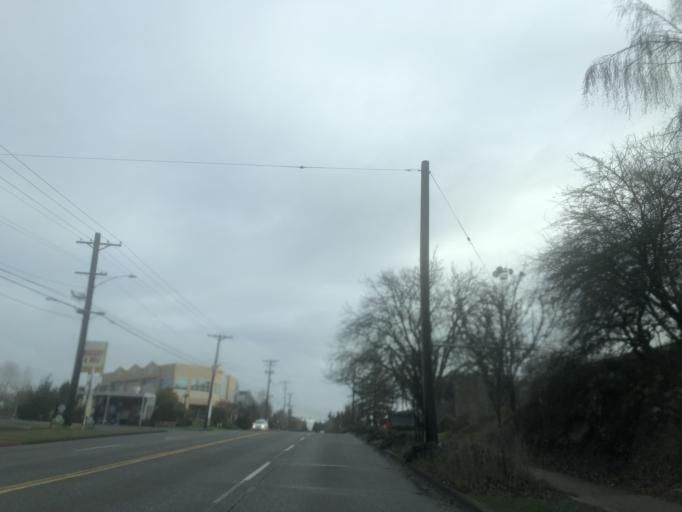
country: US
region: Washington
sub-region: Pierce County
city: Tacoma
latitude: 47.2427
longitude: -122.4698
